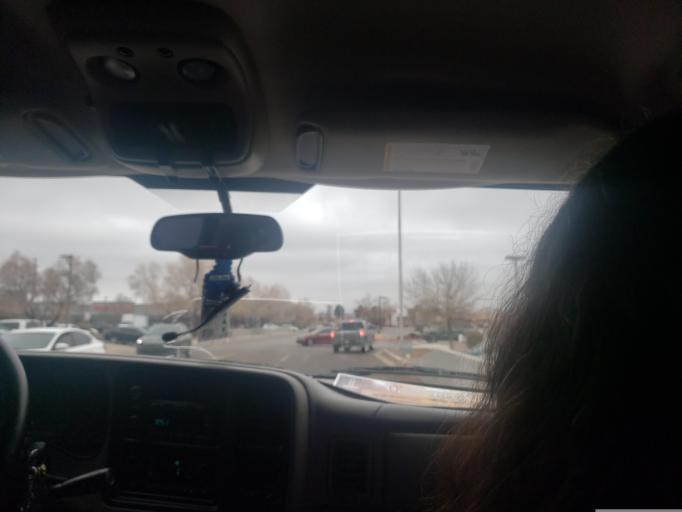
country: US
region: New Mexico
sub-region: Bernalillo County
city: Albuquerque
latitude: 35.1124
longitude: -106.7015
